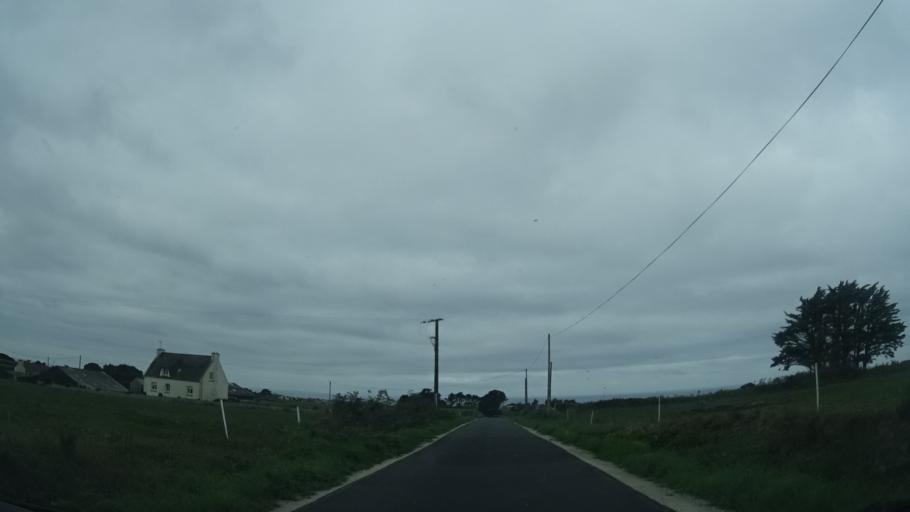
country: FR
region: Brittany
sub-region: Departement du Finistere
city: Lampaul-Plouarzel
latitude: 48.4585
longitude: -4.7485
